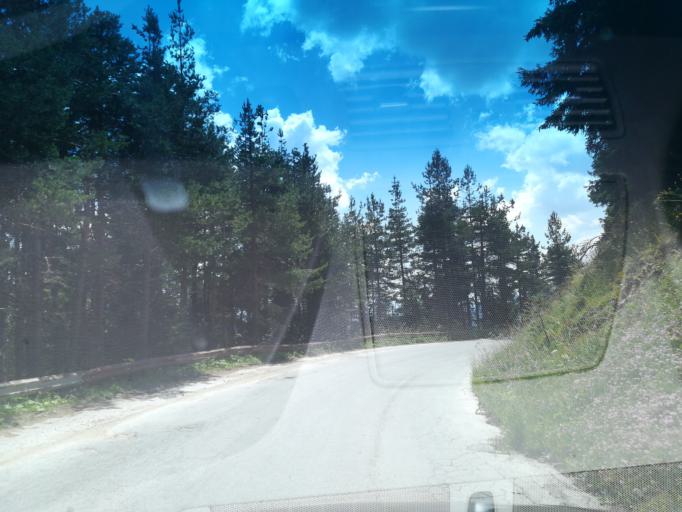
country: BG
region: Smolyan
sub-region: Obshtina Chepelare
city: Chepelare
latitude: 41.6879
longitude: 24.7579
